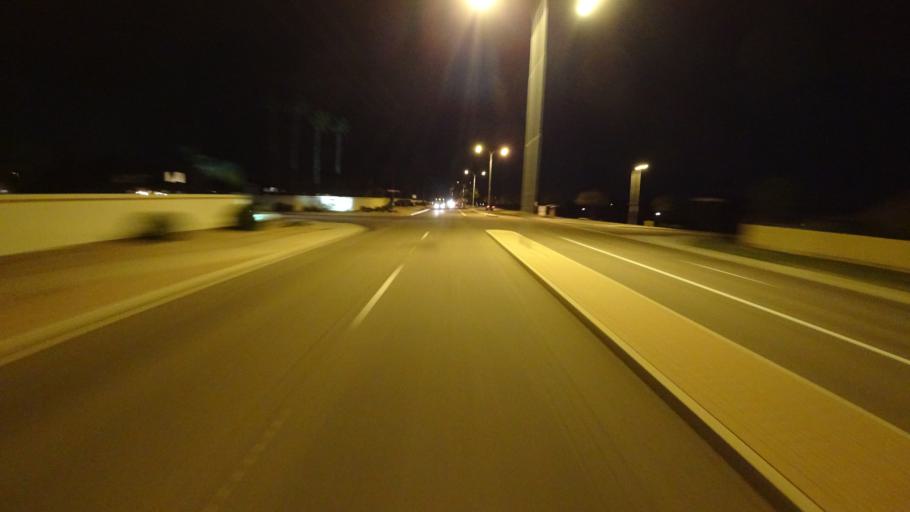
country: US
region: Arizona
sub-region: Maricopa County
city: Guadalupe
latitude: 33.3161
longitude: -111.9456
